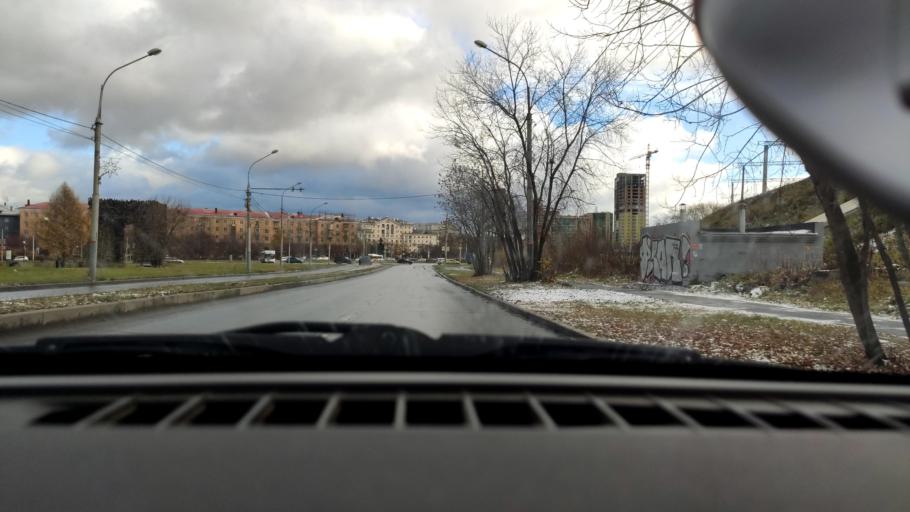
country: RU
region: Perm
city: Perm
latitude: 58.0041
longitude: 56.1910
